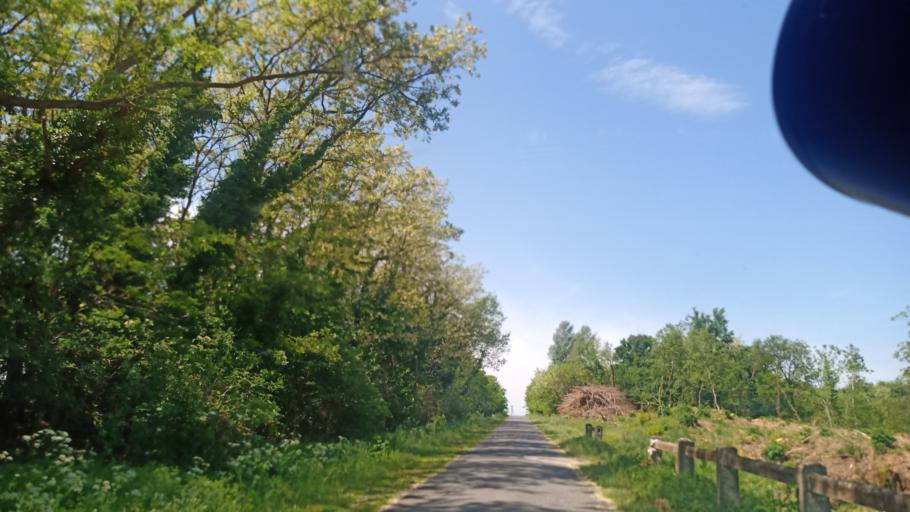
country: HU
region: Zala
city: Zalakomar
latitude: 46.6082
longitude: 17.1128
